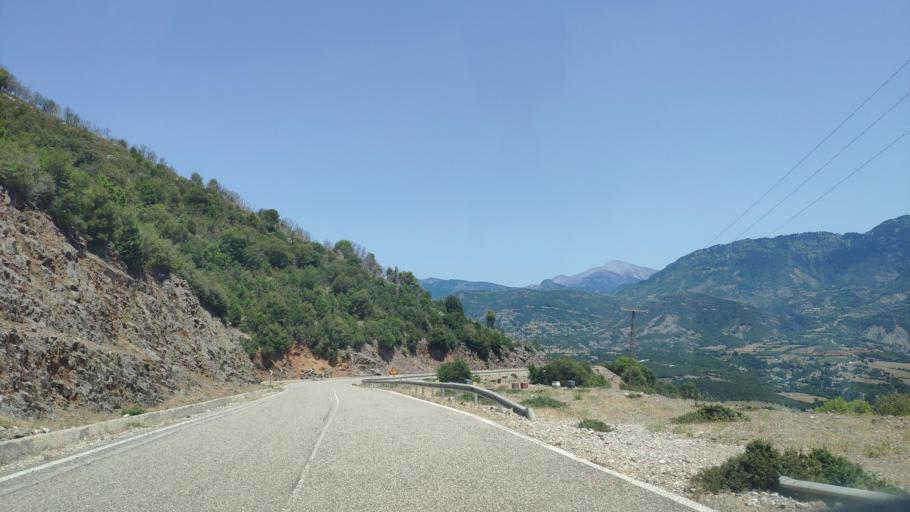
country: GR
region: Central Greece
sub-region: Nomos Evrytanias
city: Kerasochori
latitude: 39.0947
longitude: 21.4119
